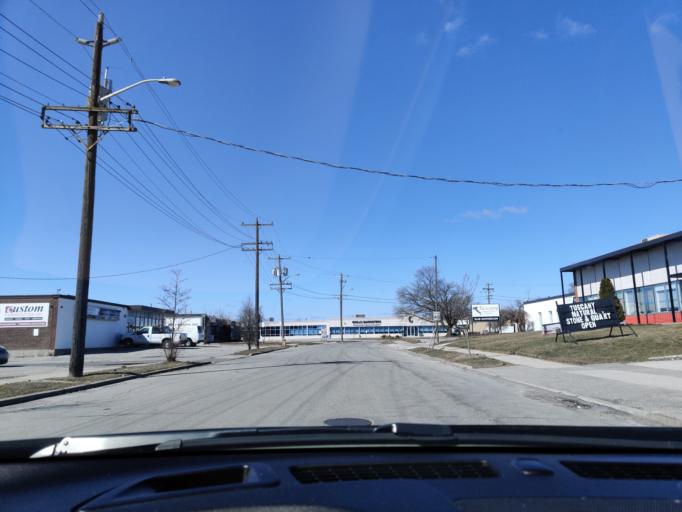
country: CA
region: Ontario
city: Toronto
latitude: 43.7147
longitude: -79.4591
